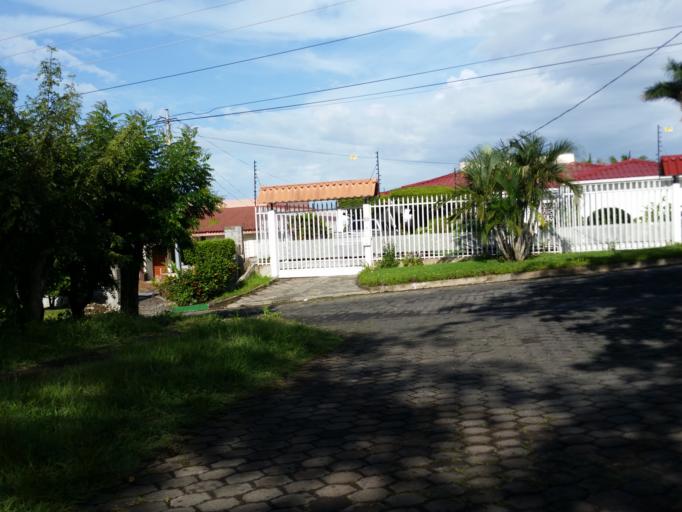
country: NI
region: Managua
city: Managua
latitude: 12.1010
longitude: -86.2572
